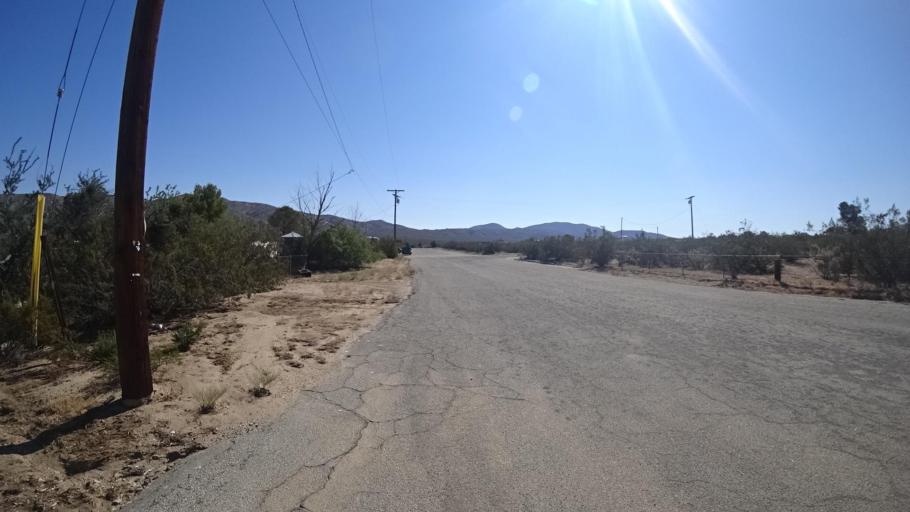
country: US
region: California
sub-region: San Diego County
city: Julian
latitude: 33.0767
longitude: -116.4424
